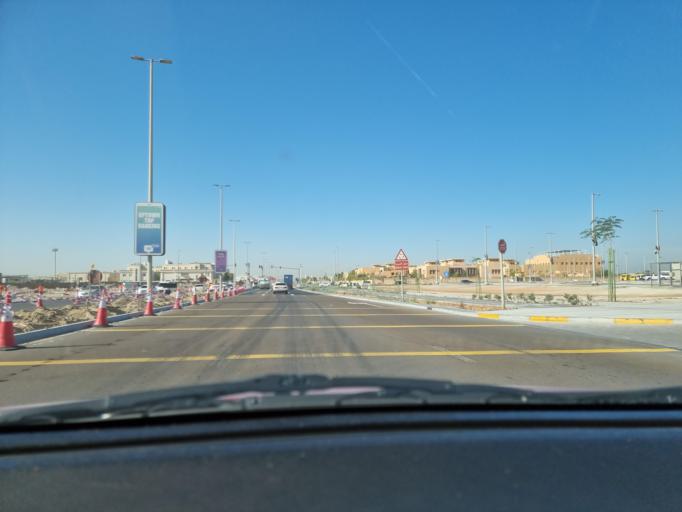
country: AE
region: Abu Dhabi
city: Abu Dhabi
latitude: 24.4341
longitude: 54.5786
